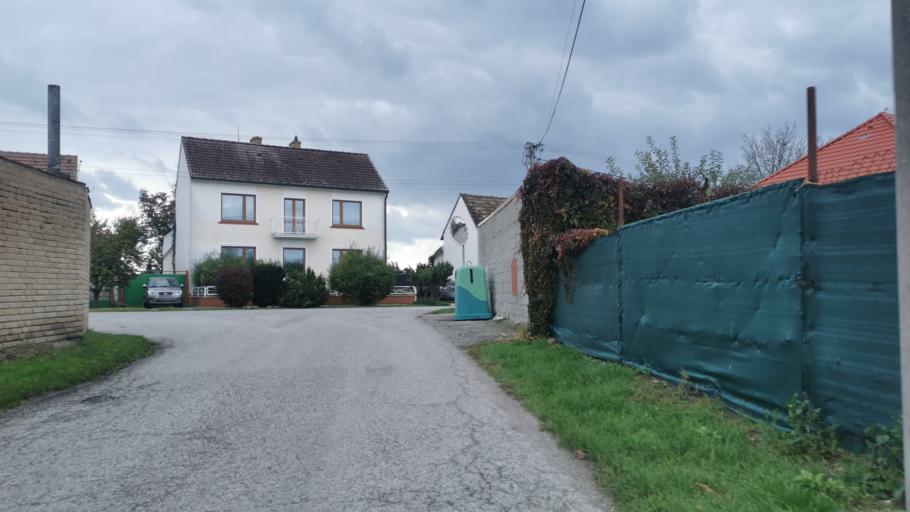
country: SK
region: Trnavsky
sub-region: Okres Skalica
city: Holic
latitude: 48.8300
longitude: 17.1728
